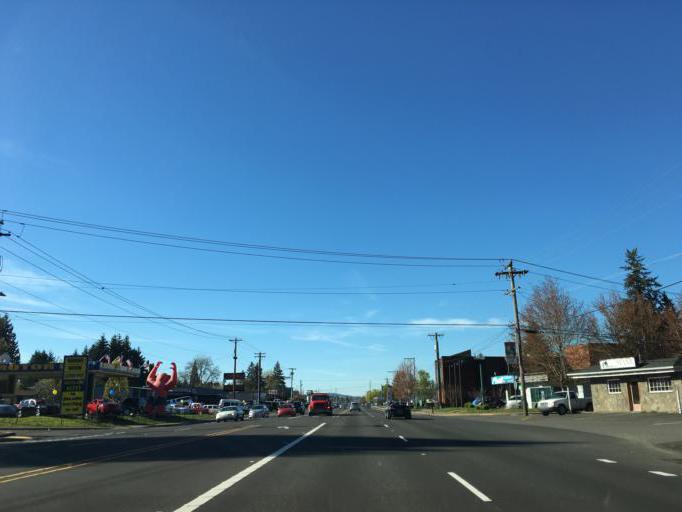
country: US
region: Oregon
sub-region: Clackamas County
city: Jennings Lodge
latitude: 45.3866
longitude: -122.6093
